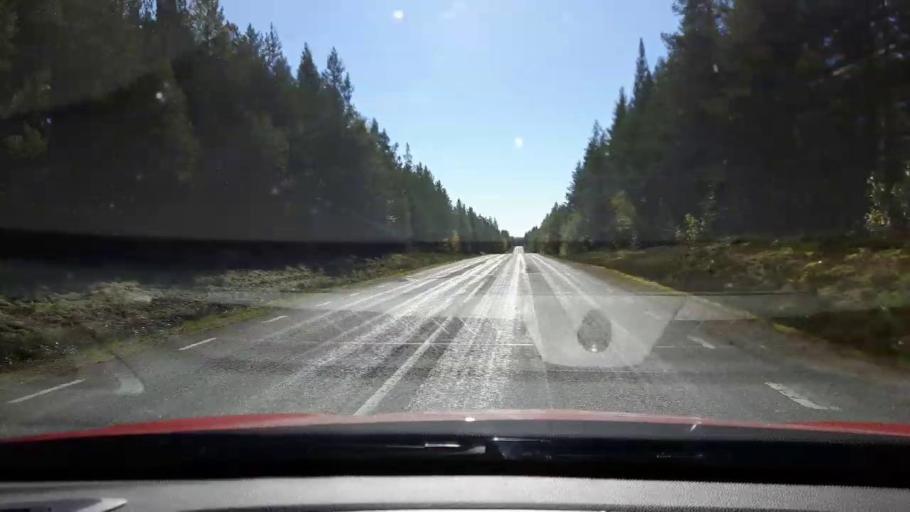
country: SE
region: Jaemtland
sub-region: Harjedalens Kommun
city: Sveg
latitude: 62.3496
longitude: 14.0312
